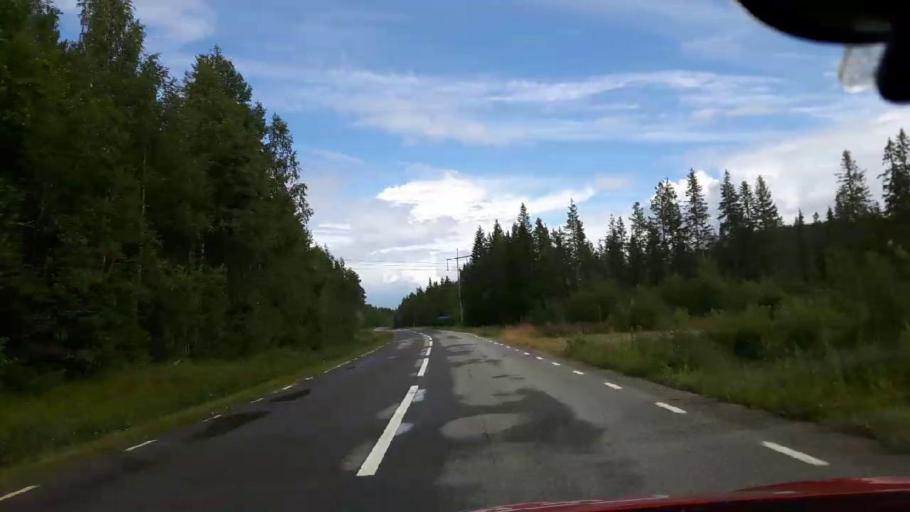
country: SE
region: Jaemtland
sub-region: Stroemsunds Kommun
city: Stroemsund
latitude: 64.3346
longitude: 14.9808
